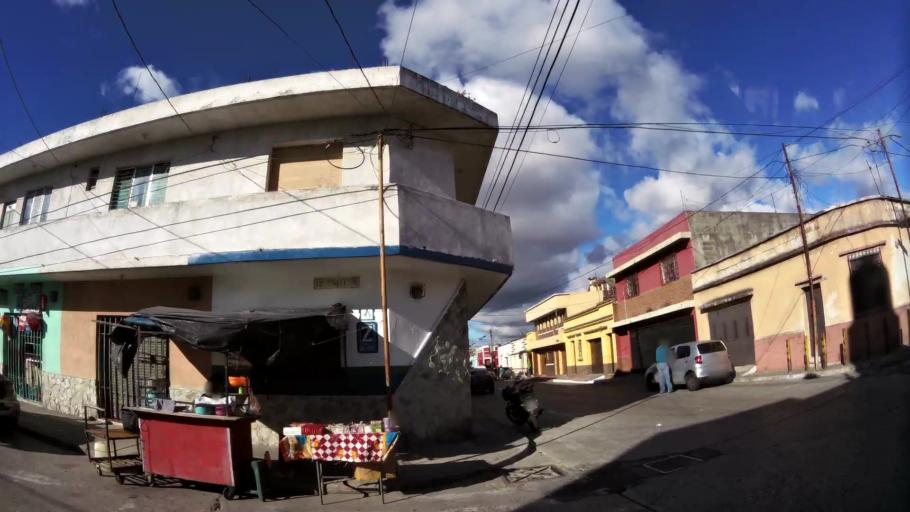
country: GT
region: Guatemala
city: Guatemala City
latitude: 14.6349
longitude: -90.5028
